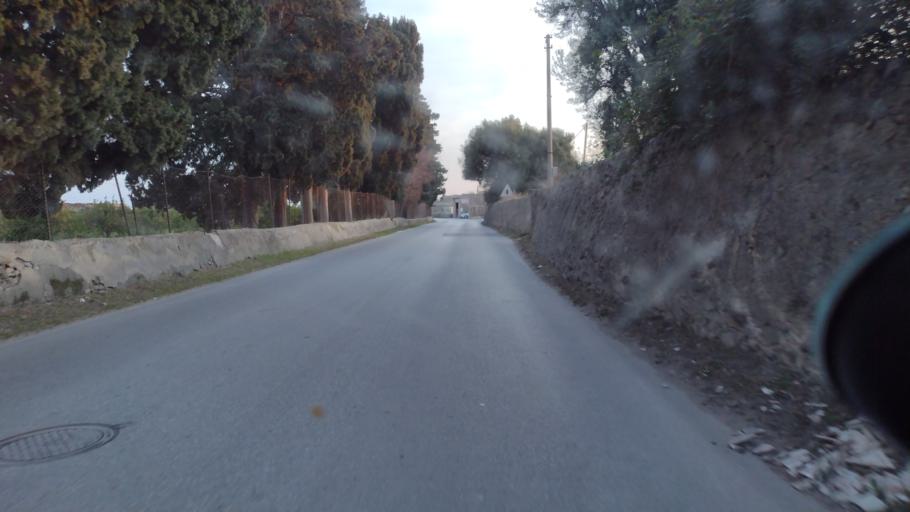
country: IT
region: Sicily
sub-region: Provincia di Siracusa
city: Avola
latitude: 36.9000
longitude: 15.1349
